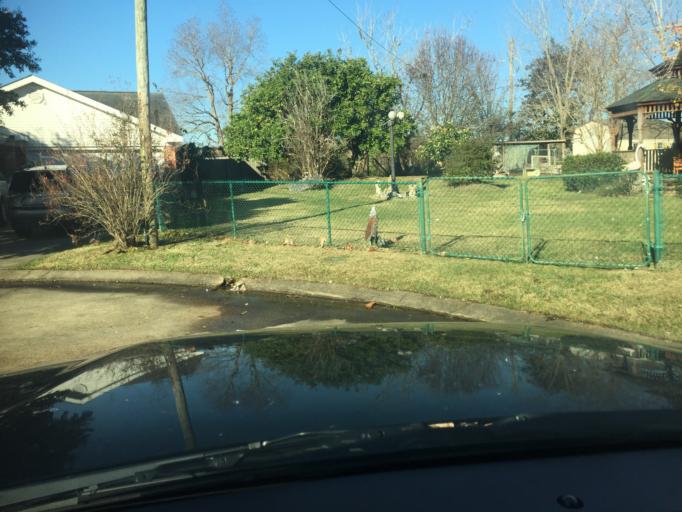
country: US
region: Louisiana
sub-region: Saint Tammany Parish
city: Slidell
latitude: 30.2536
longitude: -89.7601
